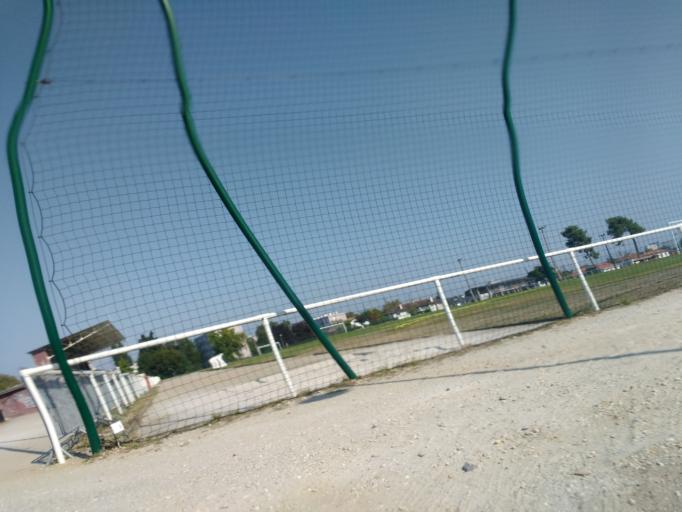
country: FR
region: Aquitaine
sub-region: Departement de la Gironde
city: Pessac
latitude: 44.8119
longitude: -0.6310
